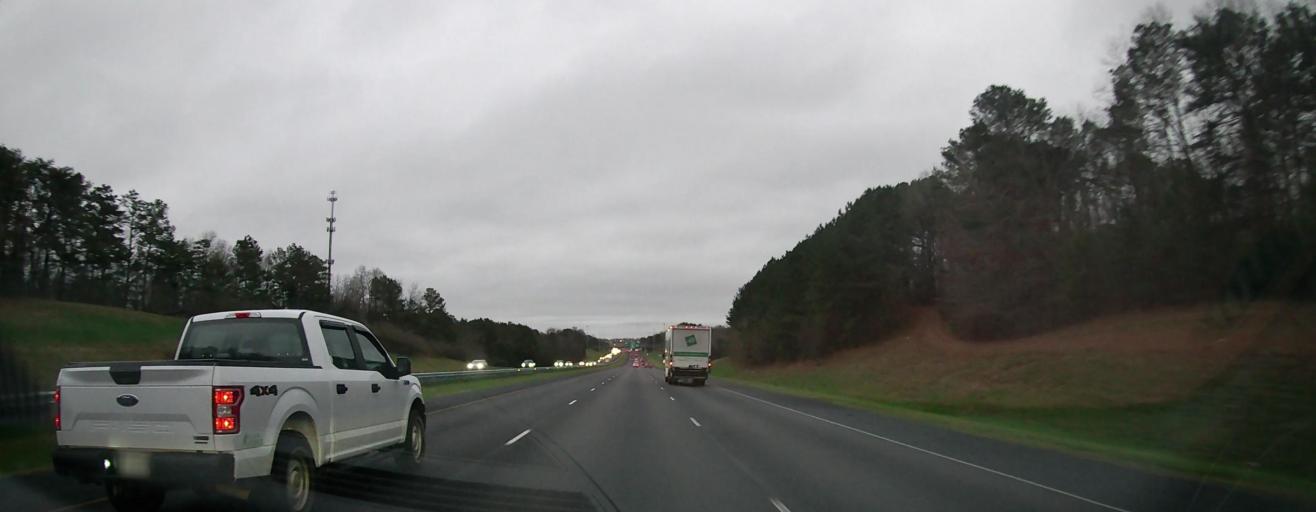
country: US
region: Alabama
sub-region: Jefferson County
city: Gardendale
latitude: 33.6301
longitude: -86.8223
